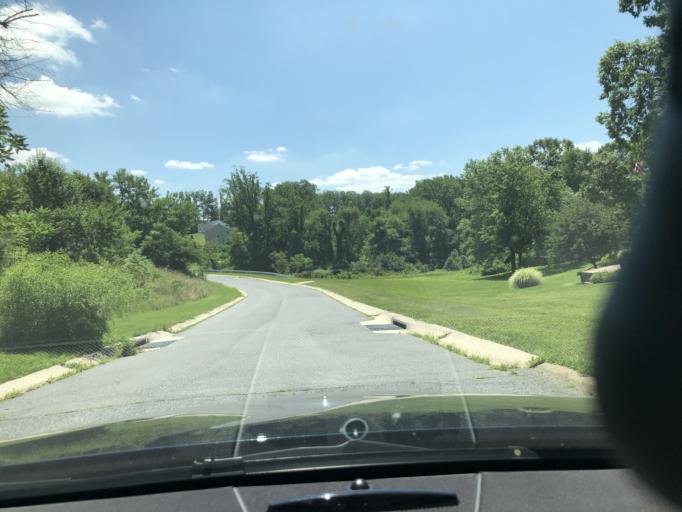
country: US
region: Maryland
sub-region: Carroll County
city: Westminster
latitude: 39.5524
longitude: -76.9689
